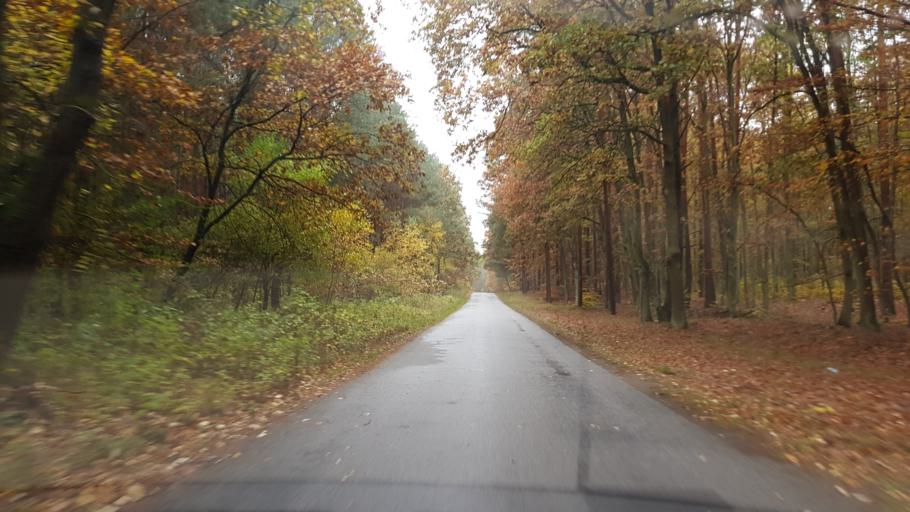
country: PL
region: West Pomeranian Voivodeship
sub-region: Powiat gryfinski
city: Chojna
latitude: 53.0548
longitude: 14.4998
